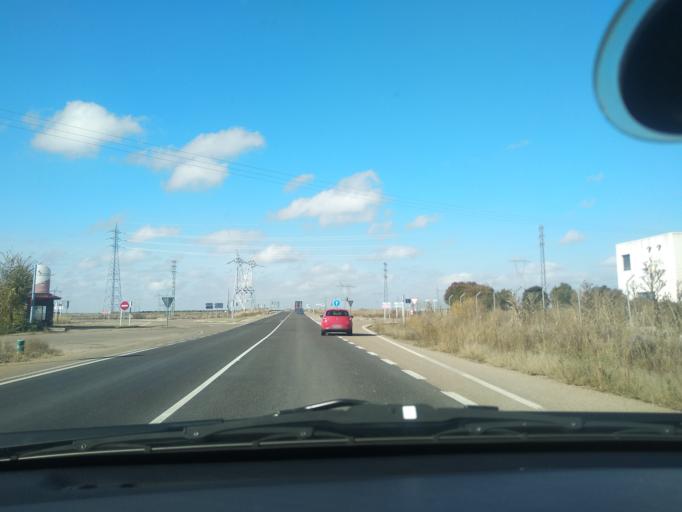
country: ES
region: Castille and Leon
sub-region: Provincia de Valladolid
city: Valdenebro de los Valles
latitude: 41.7862
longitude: -4.9425
